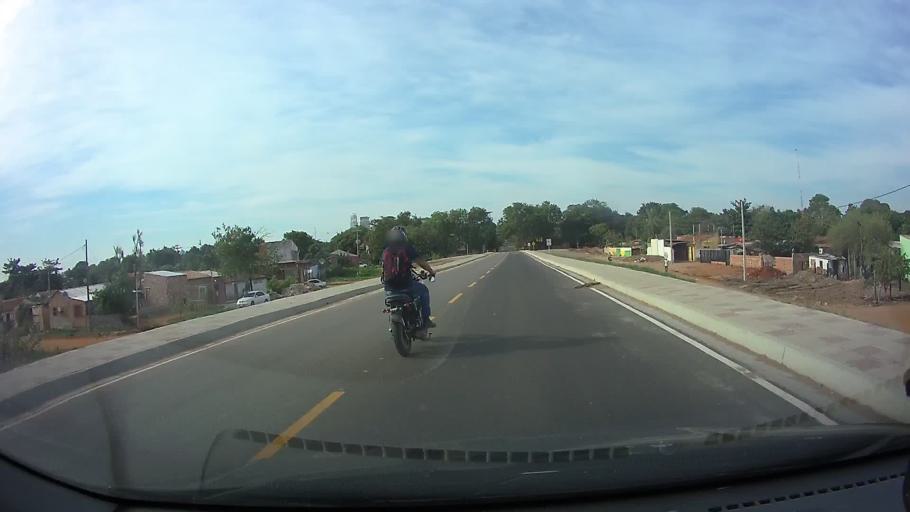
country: PY
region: Asuncion
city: Asuncion
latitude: -25.2513
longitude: -57.5901
